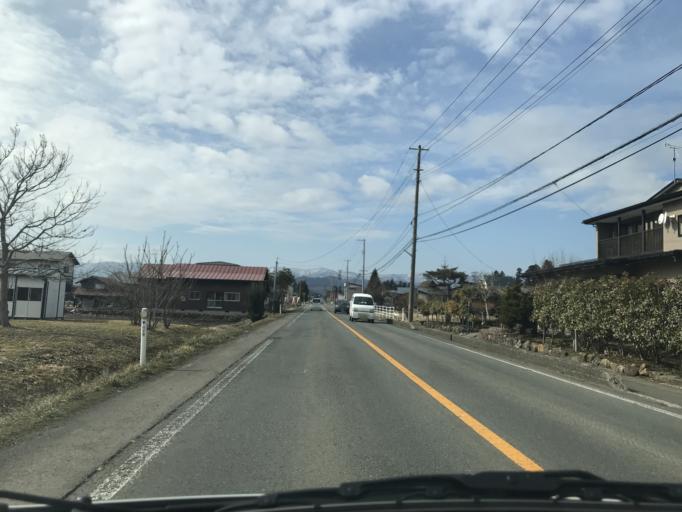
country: JP
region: Iwate
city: Hanamaki
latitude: 39.3824
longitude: 141.0747
